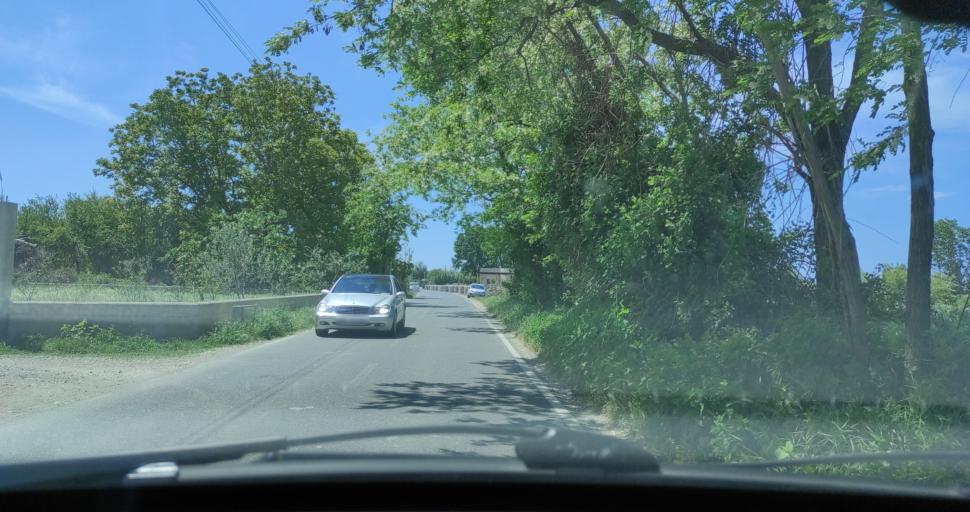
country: AL
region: Lezhe
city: Lezhe
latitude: 41.7615
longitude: 19.6306
